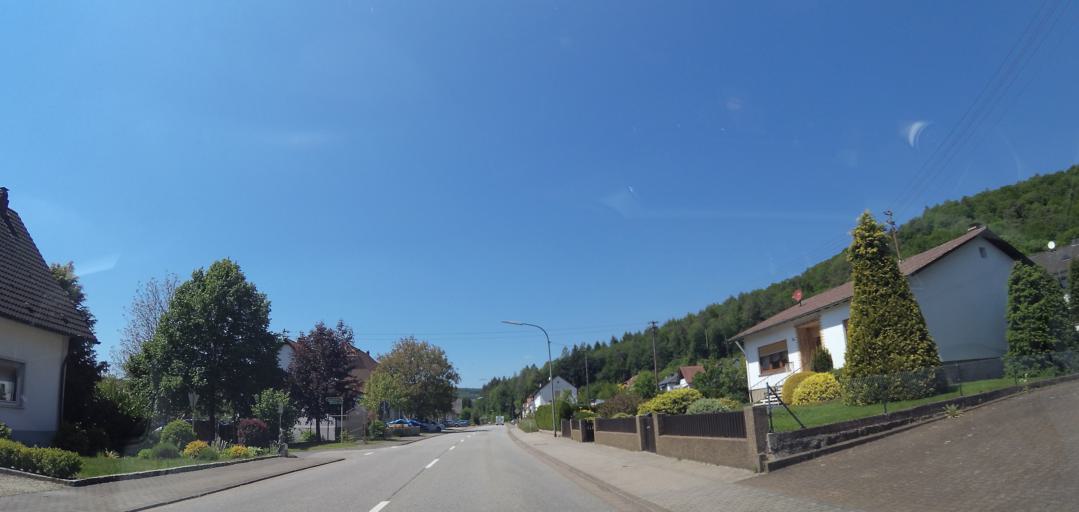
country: DE
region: Saarland
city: Losheim
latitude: 49.4504
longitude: 6.7602
